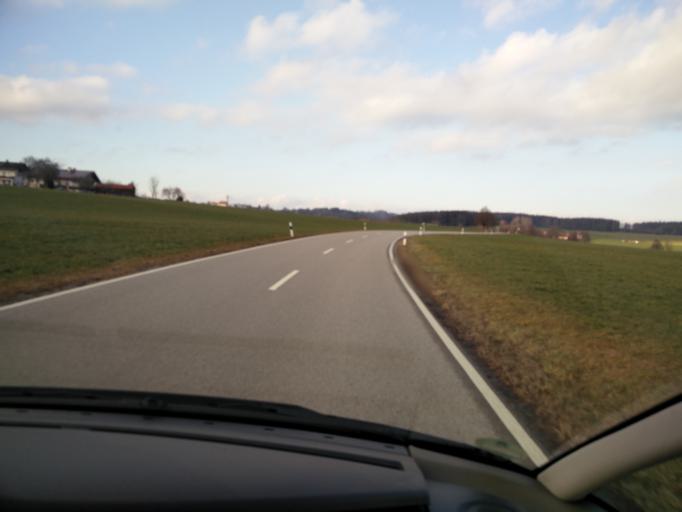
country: DE
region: Bavaria
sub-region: Upper Bavaria
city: Hoslwang
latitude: 47.9378
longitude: 12.3417
